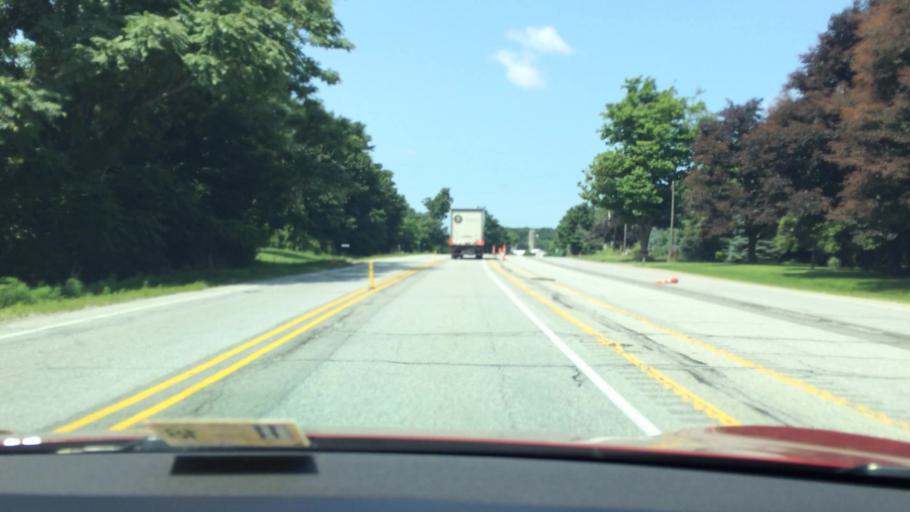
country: US
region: Indiana
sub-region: LaPorte County
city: LaPorte
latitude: 41.6724
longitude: -86.6393
